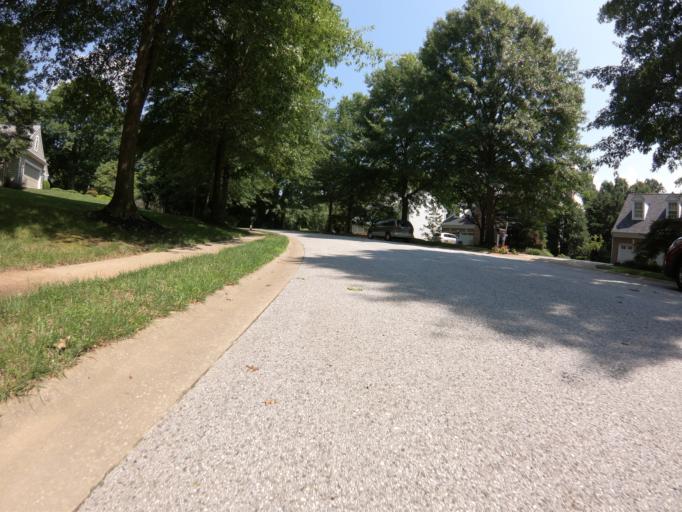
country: US
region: Maryland
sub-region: Howard County
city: Columbia
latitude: 39.2491
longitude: -76.8483
